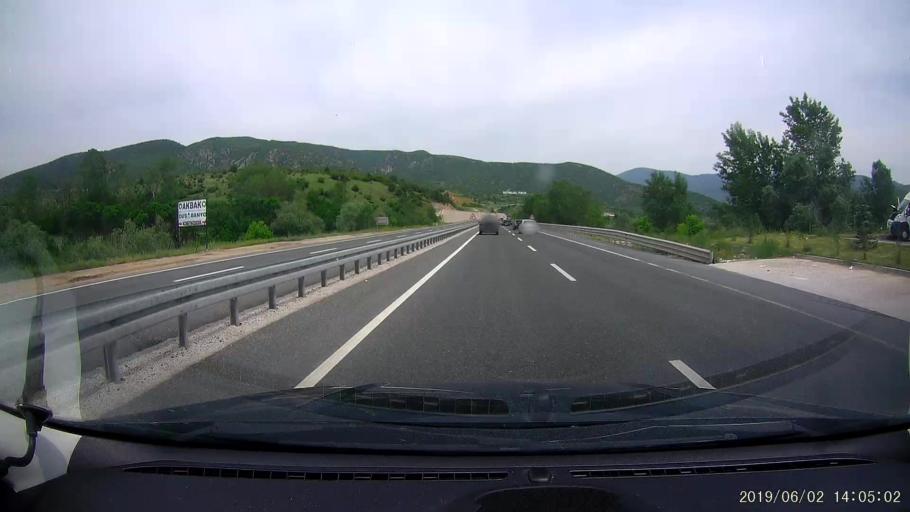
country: TR
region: Cankiri
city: Ilgaz
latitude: 40.9029
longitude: 33.6623
